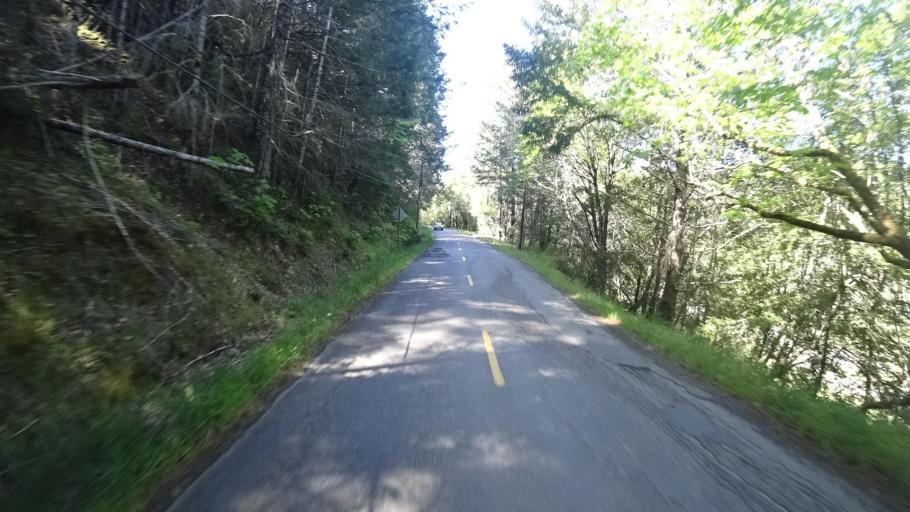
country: US
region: California
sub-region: Humboldt County
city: Rio Dell
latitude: 40.2373
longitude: -124.1344
